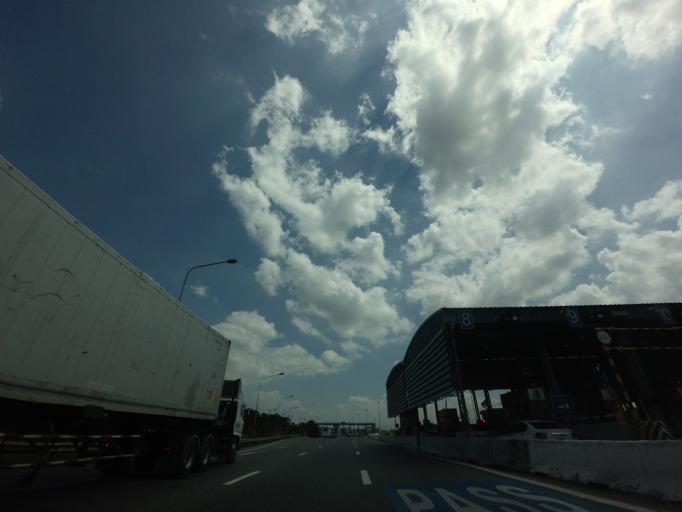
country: TH
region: Samut Prakan
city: Ban Khlong Bang Sao Thong
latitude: 13.6721
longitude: 100.8407
